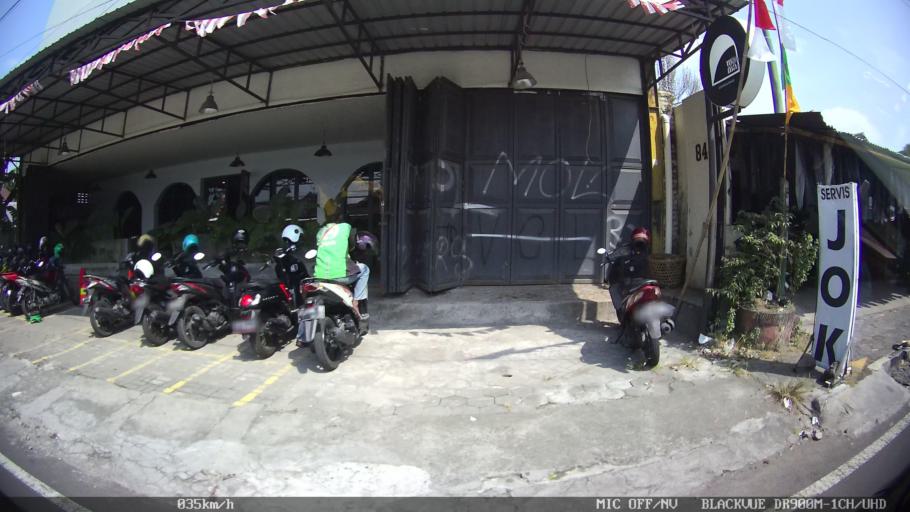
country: ID
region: Daerah Istimewa Yogyakarta
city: Yogyakarta
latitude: -7.8093
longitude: 110.3930
